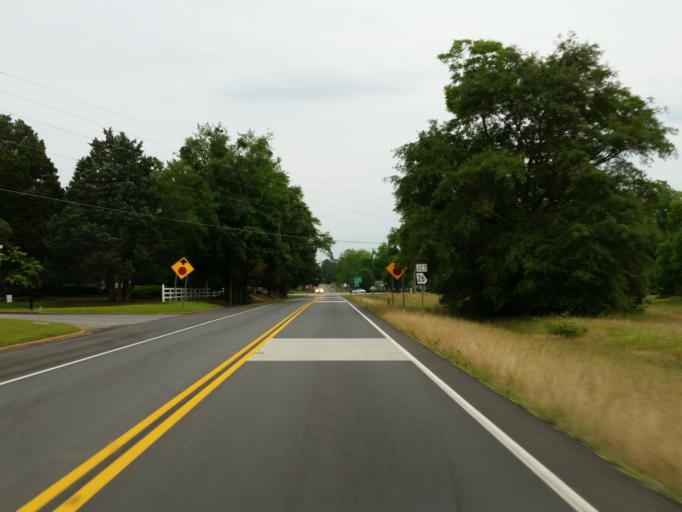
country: US
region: Georgia
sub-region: Dooly County
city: Unadilla
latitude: 32.3437
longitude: -83.7893
